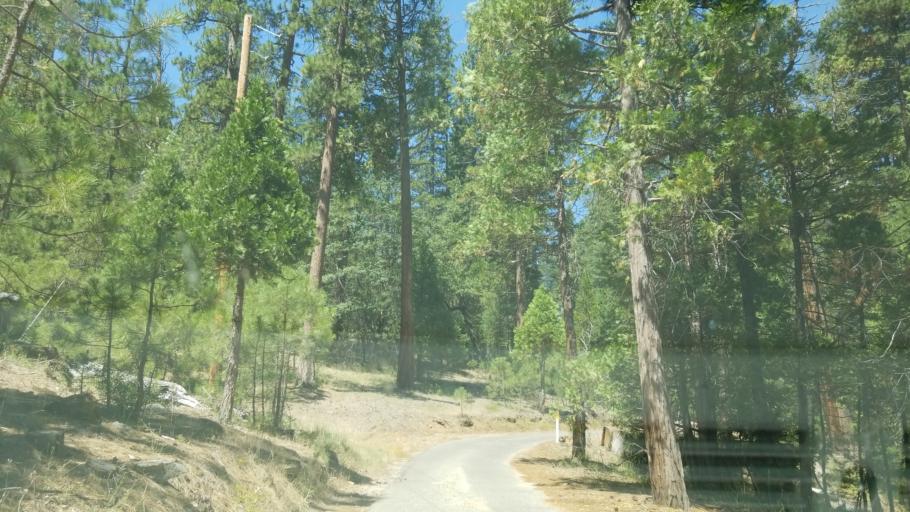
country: US
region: California
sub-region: Madera County
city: Ahwahnee
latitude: 37.5440
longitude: -119.6361
